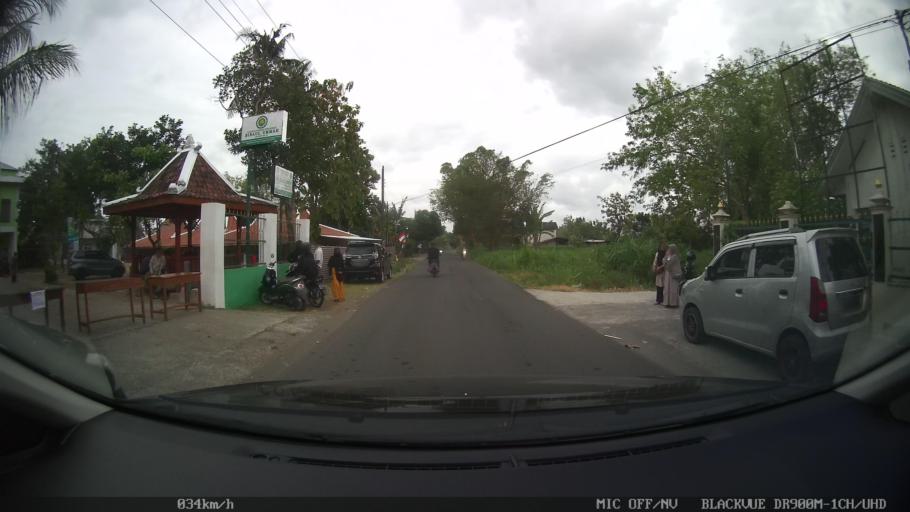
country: ID
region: Daerah Istimewa Yogyakarta
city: Sewon
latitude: -7.8756
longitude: 110.4167
